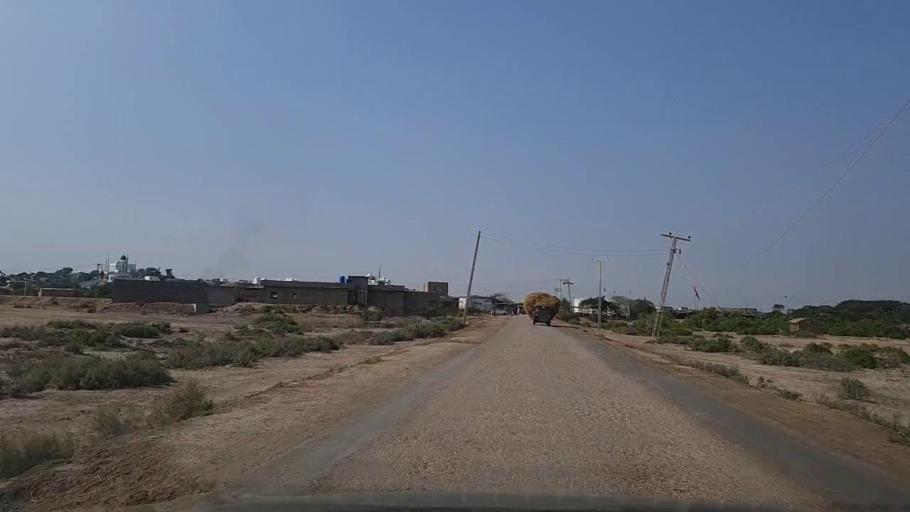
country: PK
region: Sindh
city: Thatta
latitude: 24.5580
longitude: 67.8856
